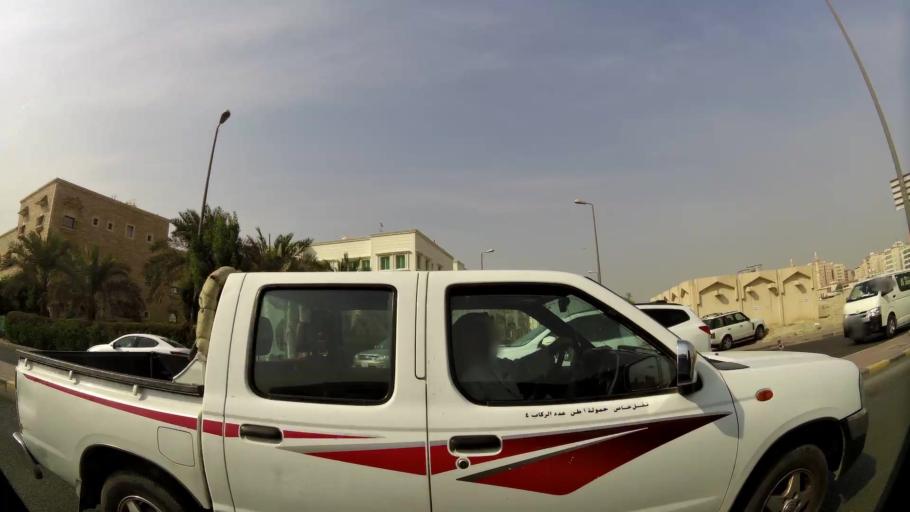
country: KW
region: Al Farwaniyah
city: Al Farwaniyah
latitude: 29.2836
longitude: 47.9535
